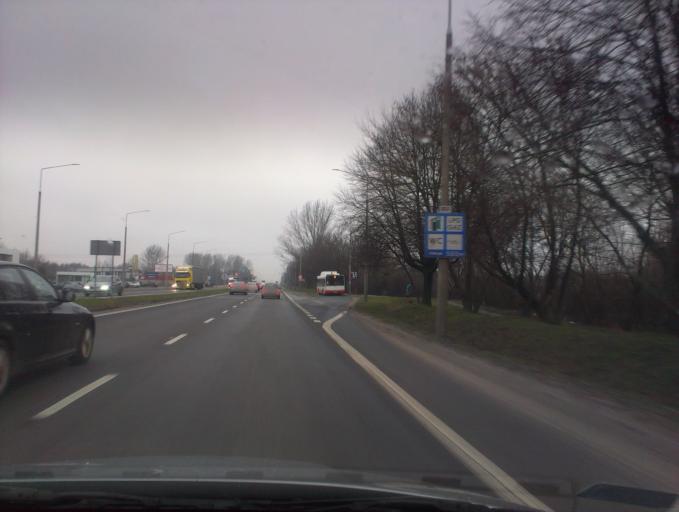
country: PL
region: Masovian Voivodeship
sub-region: Radom
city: Radom
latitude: 51.4530
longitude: 21.1423
